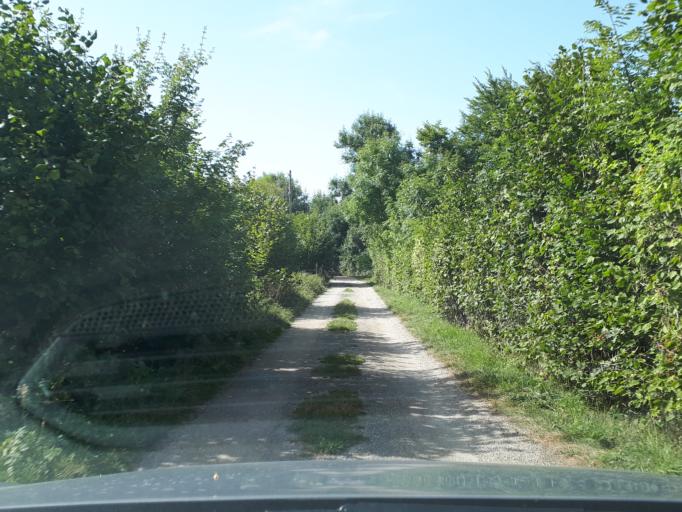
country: FR
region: Rhone-Alpes
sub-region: Departement de l'Isere
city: Pierre-Chatel
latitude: 44.9861
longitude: 5.7831
